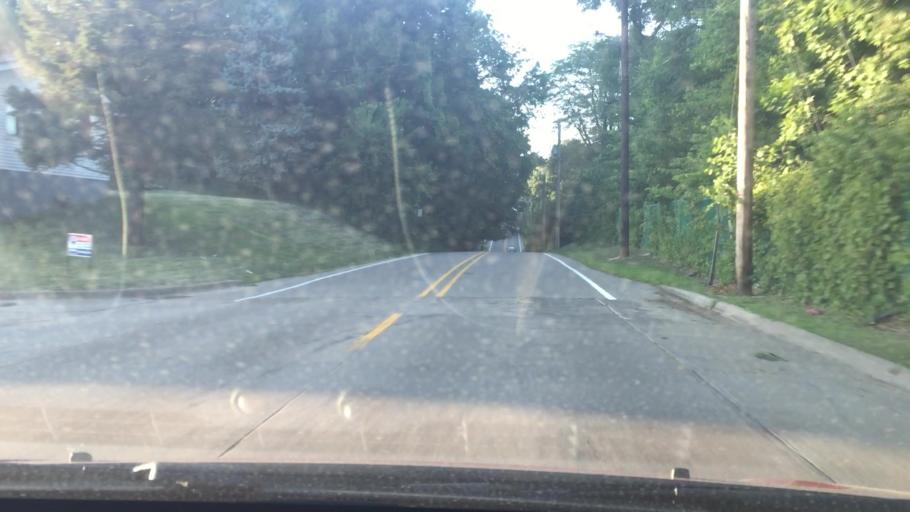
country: US
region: Iowa
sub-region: Muscatine County
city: Muscatine
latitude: 41.4262
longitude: -91.0650
